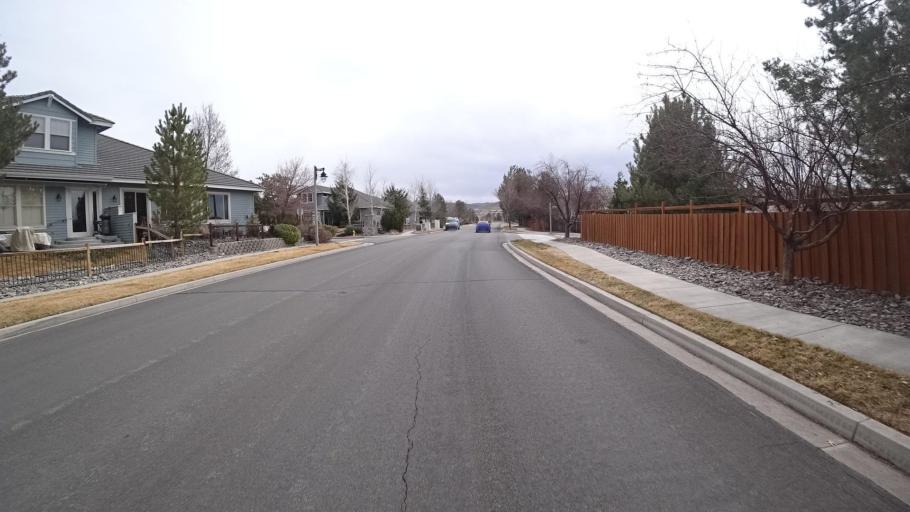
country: US
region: Nevada
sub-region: Washoe County
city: Spanish Springs
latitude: 39.6138
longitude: -119.6917
